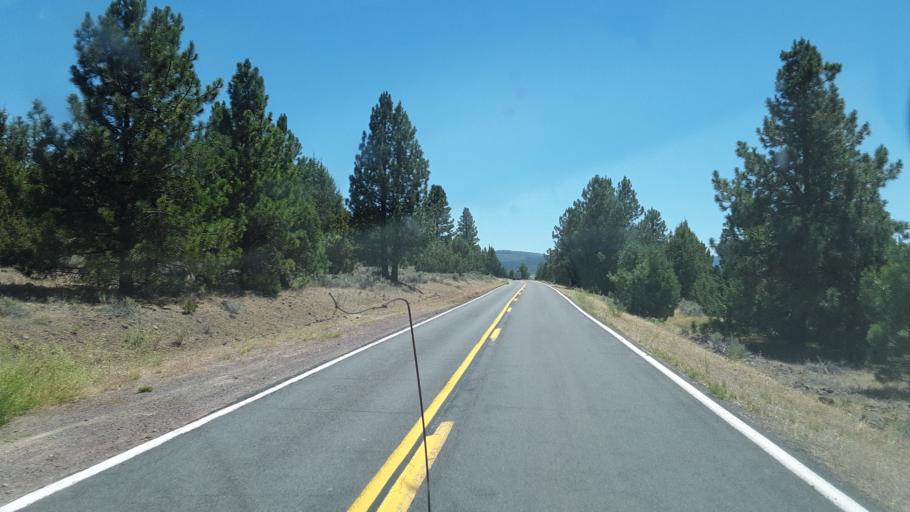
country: US
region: California
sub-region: Lassen County
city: Susanville
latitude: 40.7061
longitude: -120.6730
